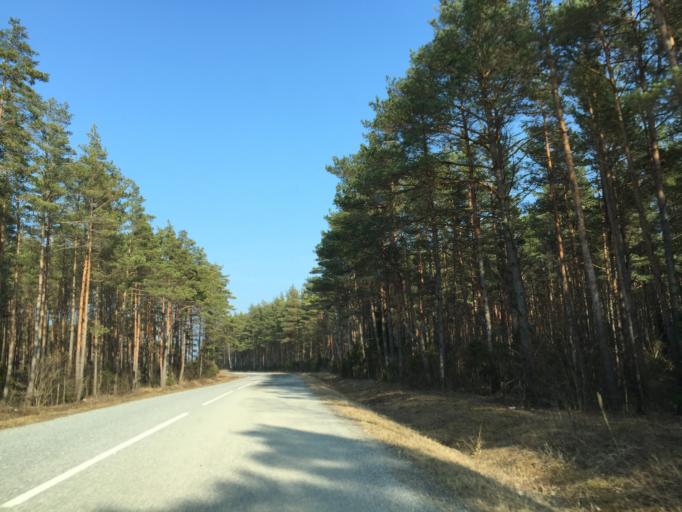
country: EE
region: Saare
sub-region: Orissaare vald
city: Orissaare
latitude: 58.5624
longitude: 23.3385
